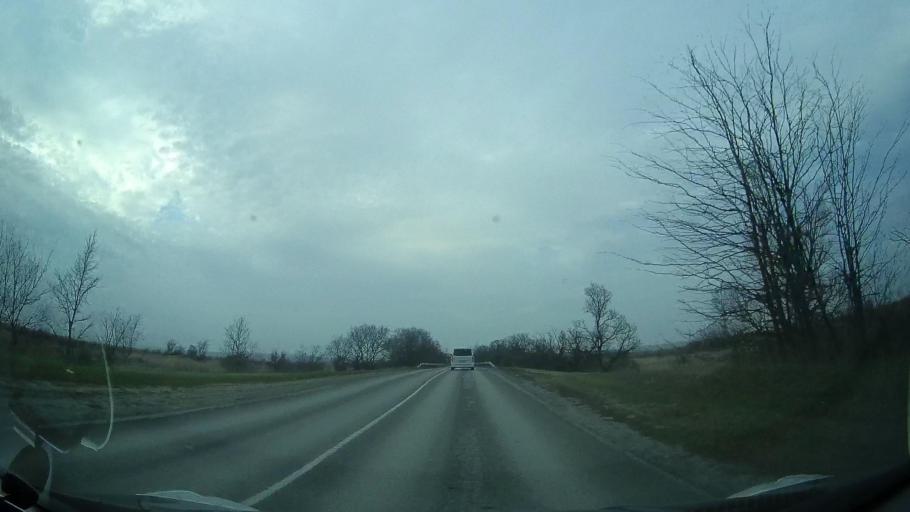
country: RU
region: Rostov
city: Ol'ginskaya
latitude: 47.2132
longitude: 39.9148
